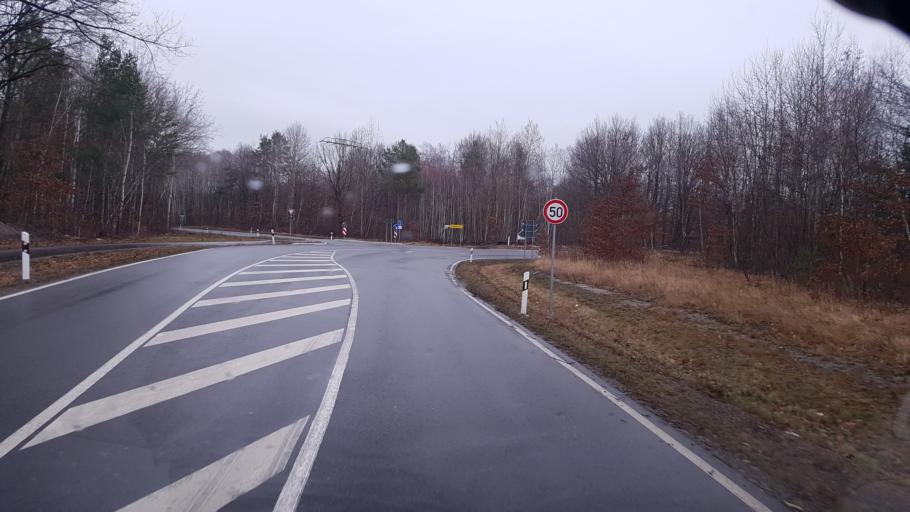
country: DE
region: Brandenburg
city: Schwarzheide
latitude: 51.5171
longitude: 13.8353
